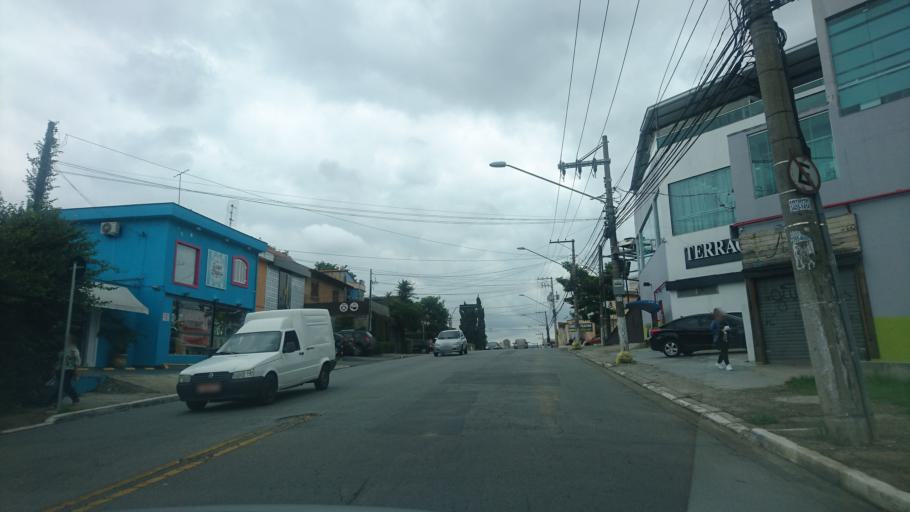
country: BR
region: Sao Paulo
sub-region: Guarulhos
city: Guarulhos
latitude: -23.4550
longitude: -46.5285
